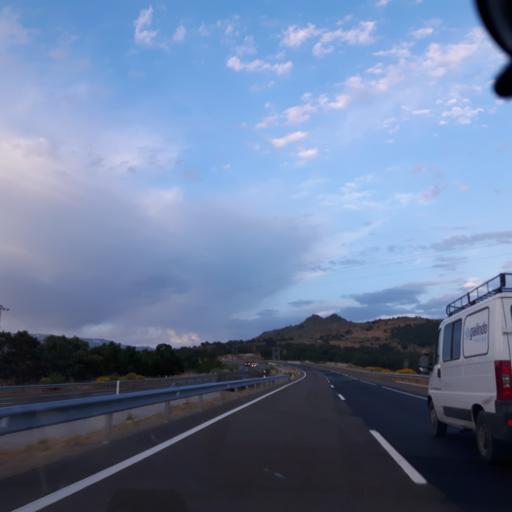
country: ES
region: Castille and Leon
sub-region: Provincia de Salamanca
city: Nava de Bejar
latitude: 40.4793
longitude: -5.6794
